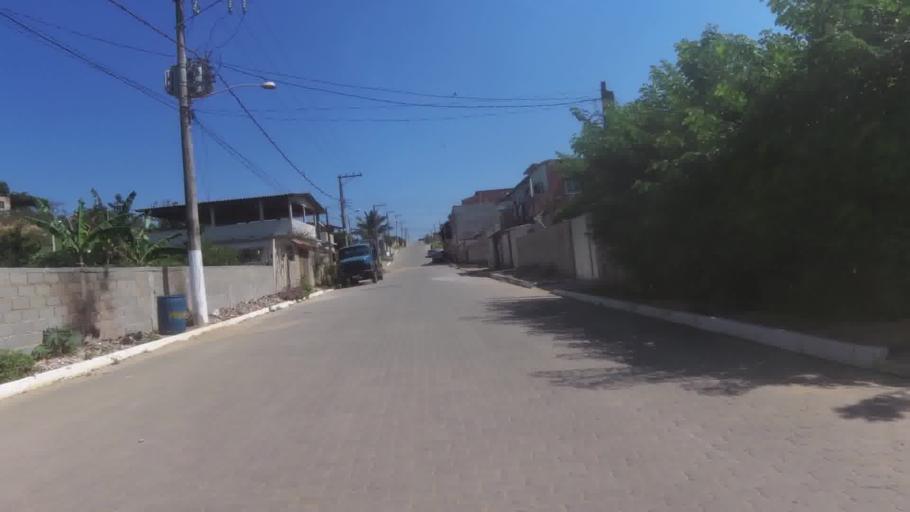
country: BR
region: Espirito Santo
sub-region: Itapemirim
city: Itapemirim
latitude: -21.0174
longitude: -40.8192
